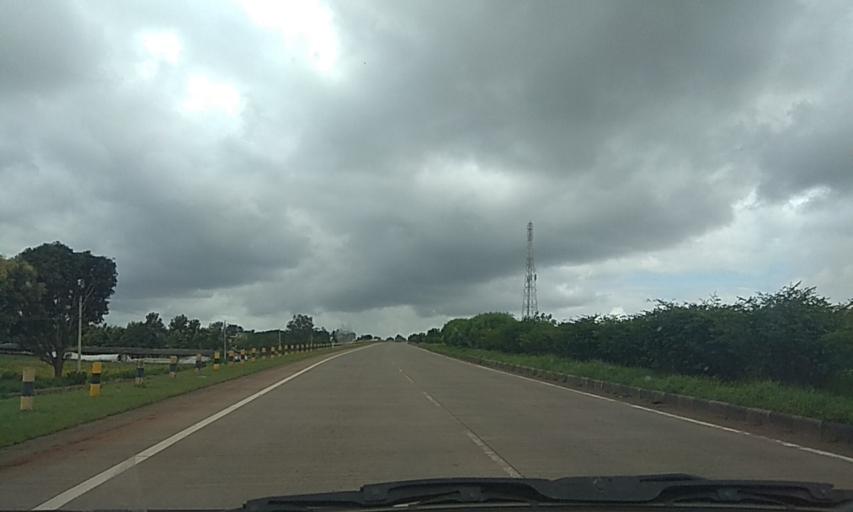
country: IN
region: Karnataka
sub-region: Belgaum
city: Sankeshwar
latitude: 16.2524
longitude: 74.4736
